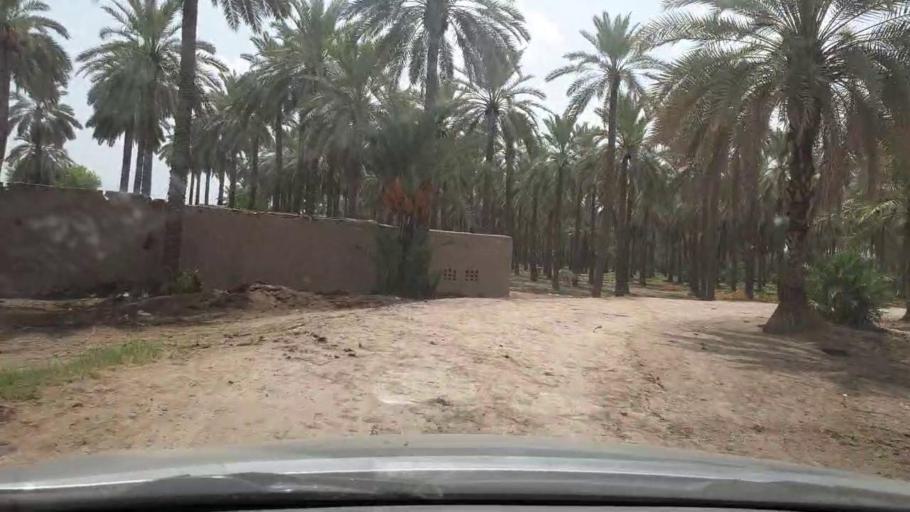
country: PK
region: Sindh
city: Kot Diji
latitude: 27.4042
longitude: 68.7535
